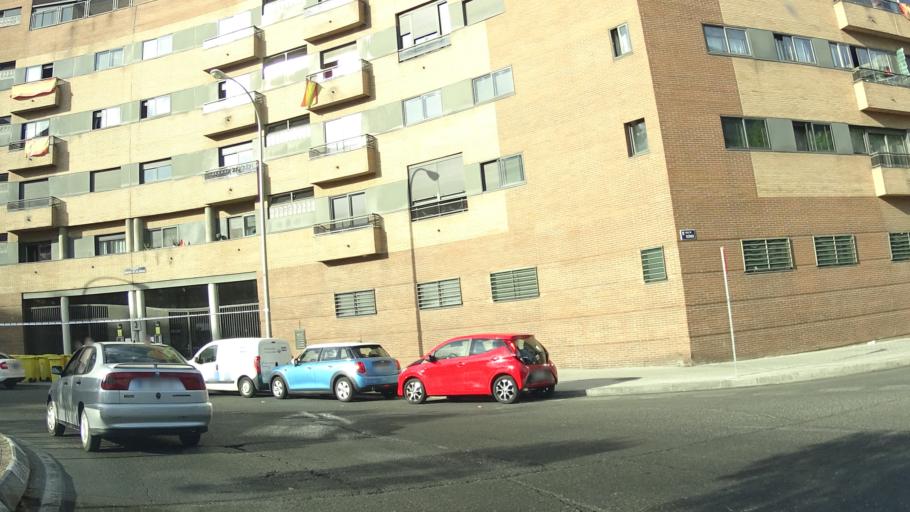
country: ES
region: Madrid
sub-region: Provincia de Madrid
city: Ciudad Lineal
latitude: 40.4472
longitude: -3.6374
